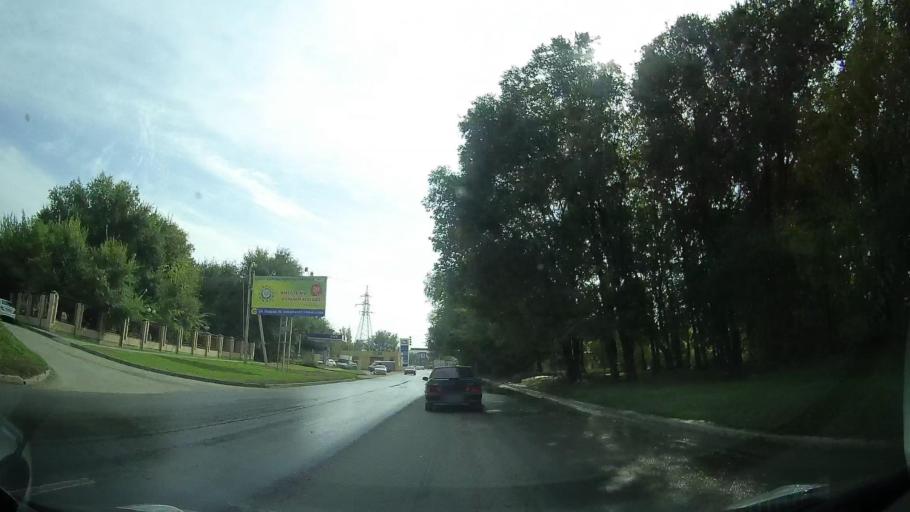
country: RU
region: Rostov
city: Severnyy
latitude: 47.2754
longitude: 39.7047
